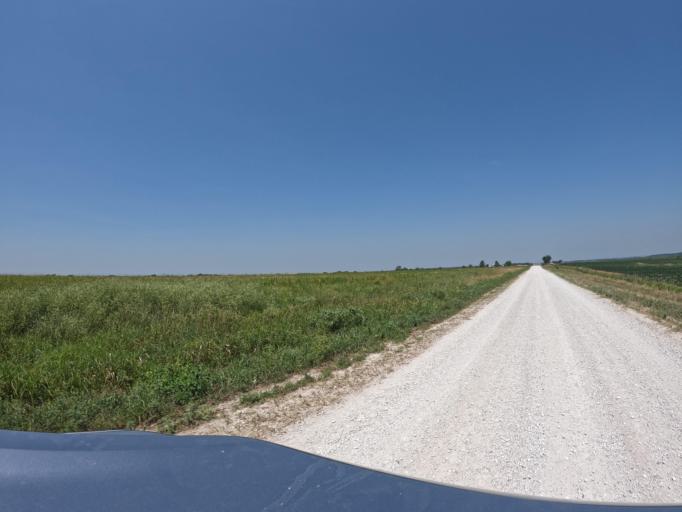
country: US
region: Iowa
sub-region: Keokuk County
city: Sigourney
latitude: 41.2704
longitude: -92.1807
